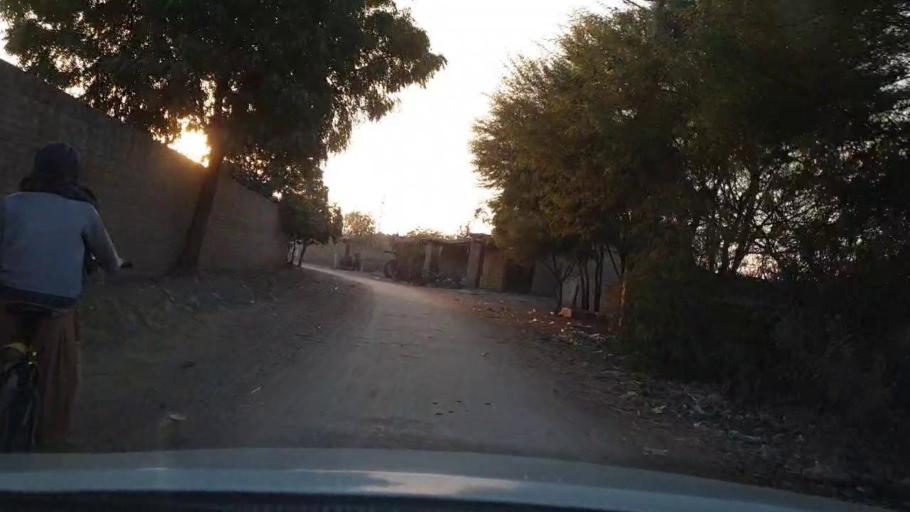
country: PK
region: Sindh
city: Tando Allahyar
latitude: 25.5239
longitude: 68.6213
